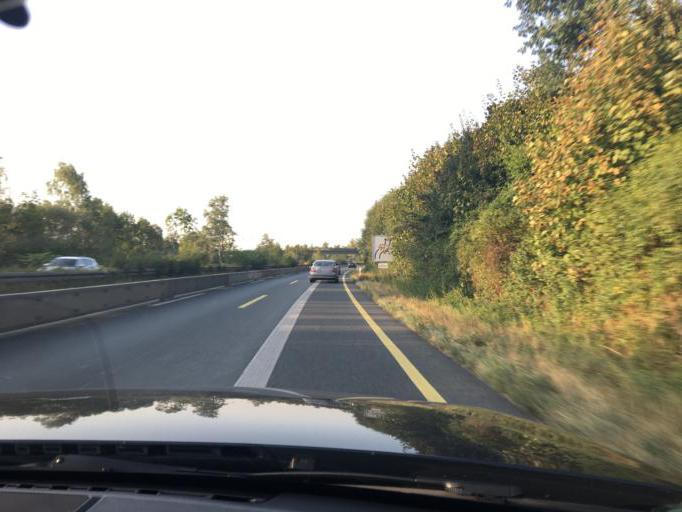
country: DE
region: Bavaria
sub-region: Upper Franconia
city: Forchheim
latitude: 49.7191
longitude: 11.0514
